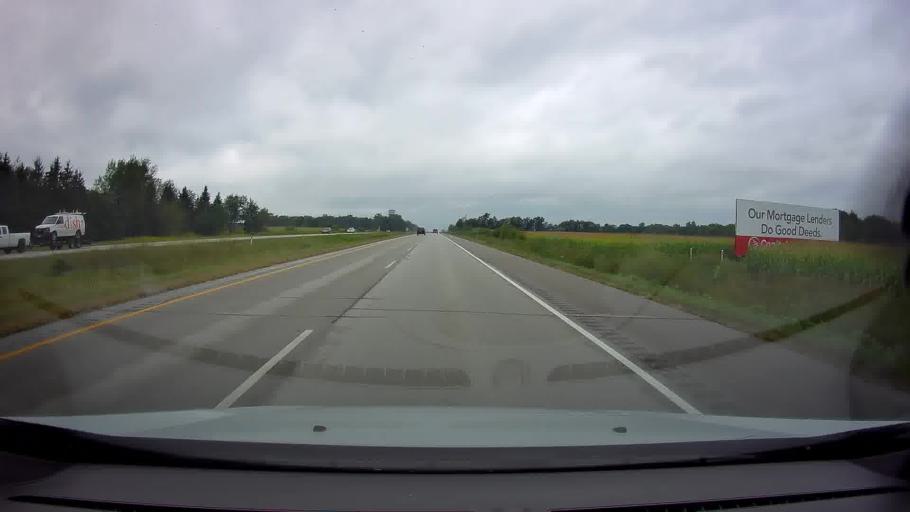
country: US
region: Wisconsin
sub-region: Brown County
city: Howard
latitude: 44.5665
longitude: -88.1444
